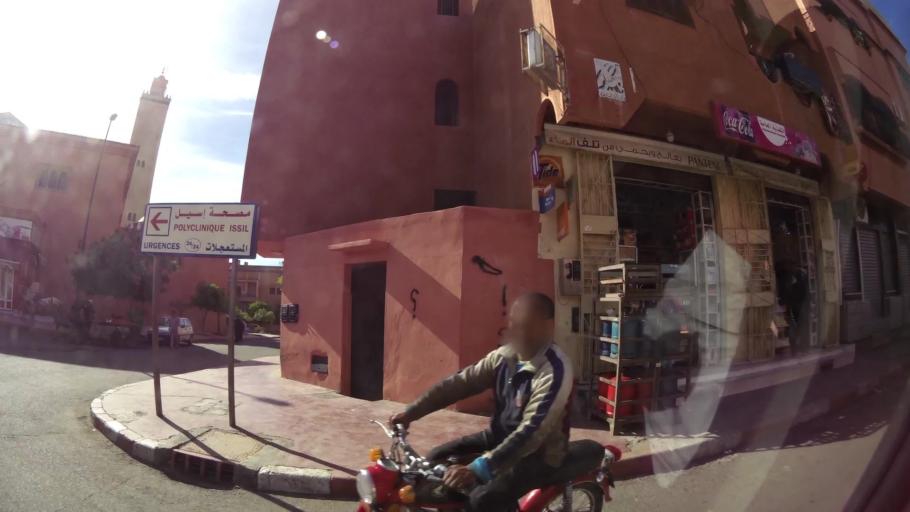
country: MA
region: Marrakech-Tensift-Al Haouz
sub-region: Marrakech
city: Marrakesh
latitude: 31.6603
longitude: -8.0119
